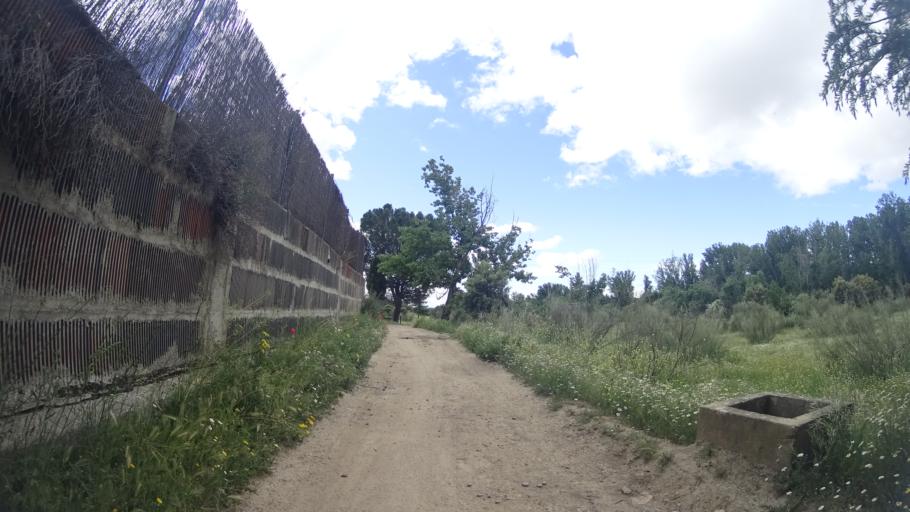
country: ES
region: Madrid
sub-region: Provincia de Madrid
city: Brunete
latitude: 40.4124
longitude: -3.9469
